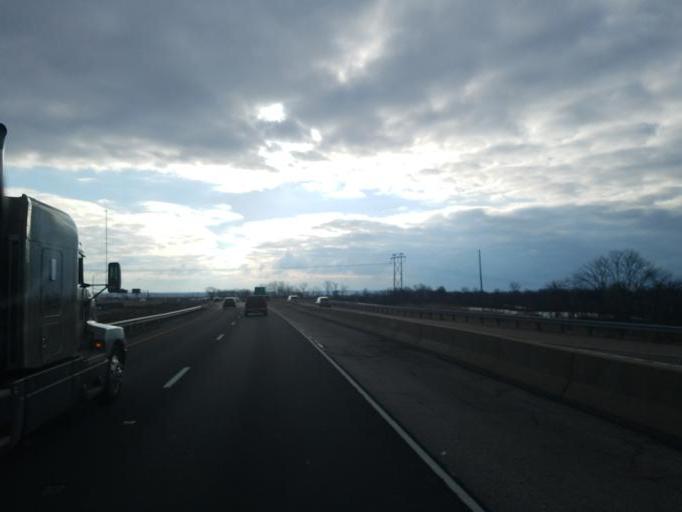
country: US
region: Illinois
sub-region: Madison County
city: Mitchell
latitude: 38.7584
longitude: -90.0915
